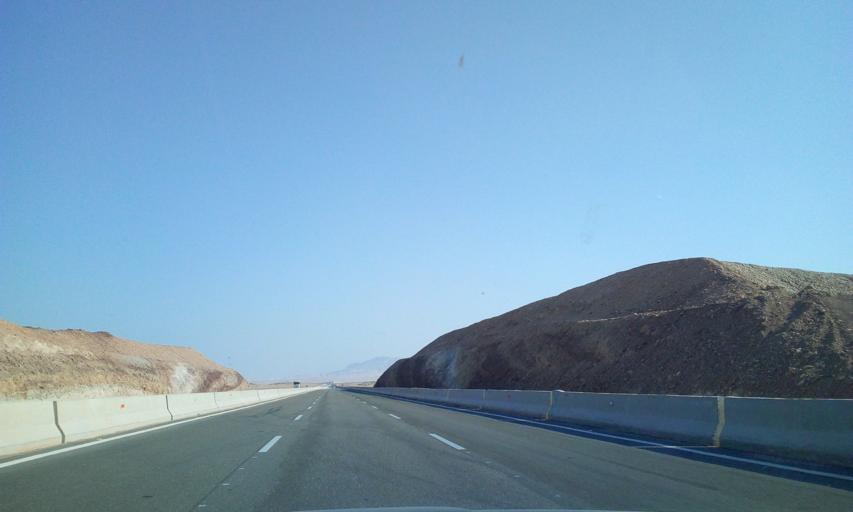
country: EG
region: As Suways
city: Ain Sukhna
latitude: 29.1629
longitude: 32.5103
